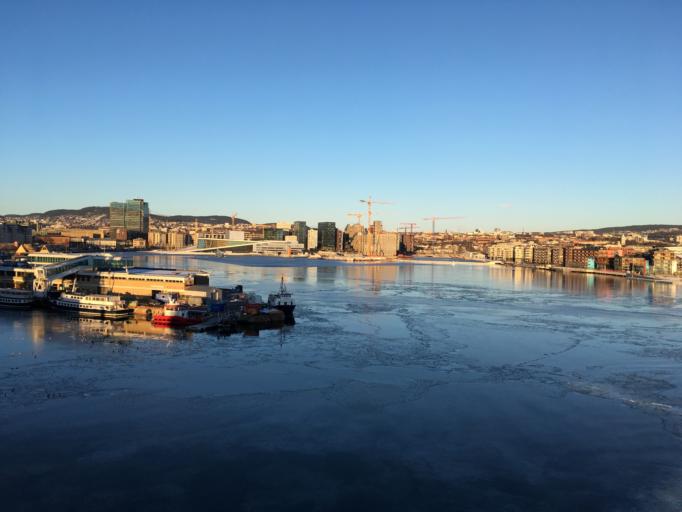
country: NO
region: Oslo
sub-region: Oslo
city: Oslo
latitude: 59.9007
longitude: 10.7415
